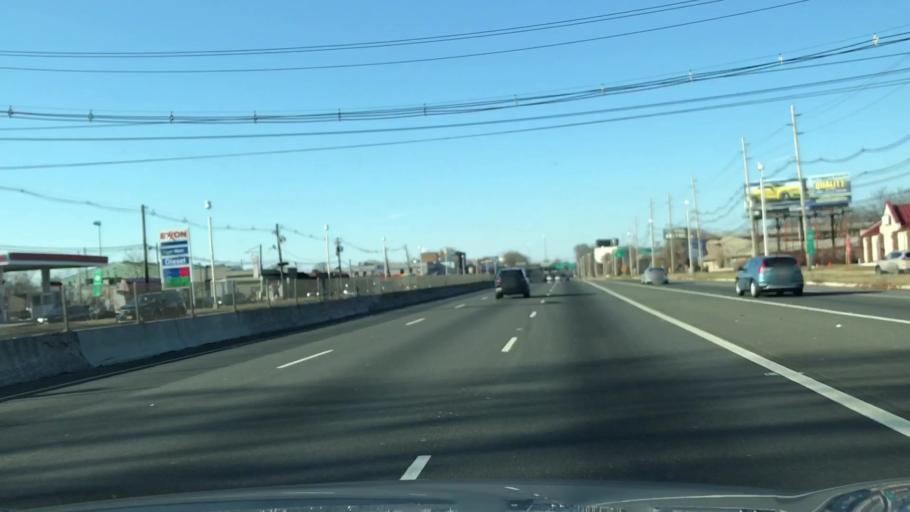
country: US
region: New Jersey
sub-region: Hudson County
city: Secaucus
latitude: 40.7907
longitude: -74.0531
